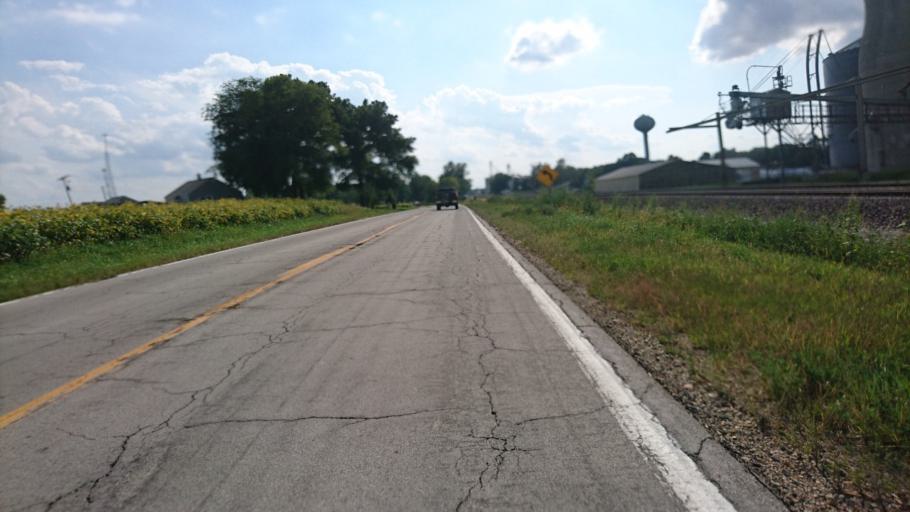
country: US
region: Illinois
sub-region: Logan County
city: Atlanta
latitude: 40.3195
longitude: -89.1639
